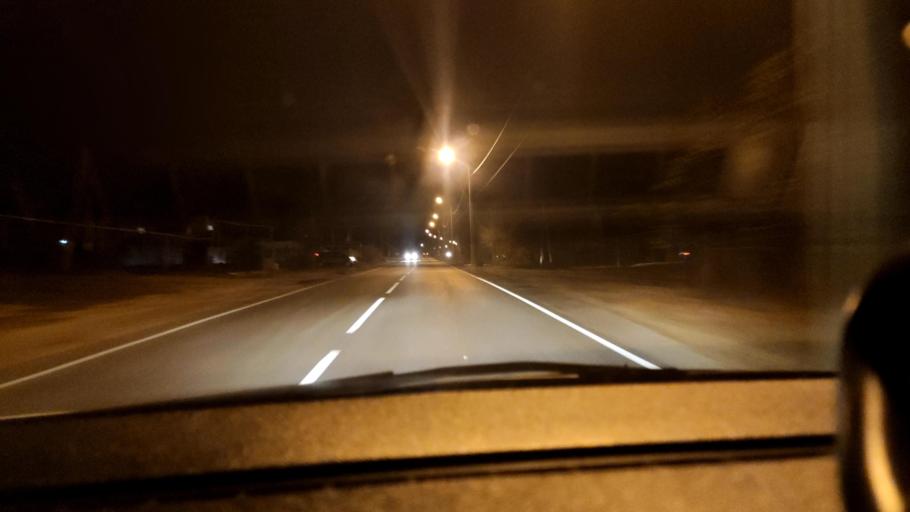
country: RU
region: Voronezj
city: Shilovo
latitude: 51.5702
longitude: 39.0444
